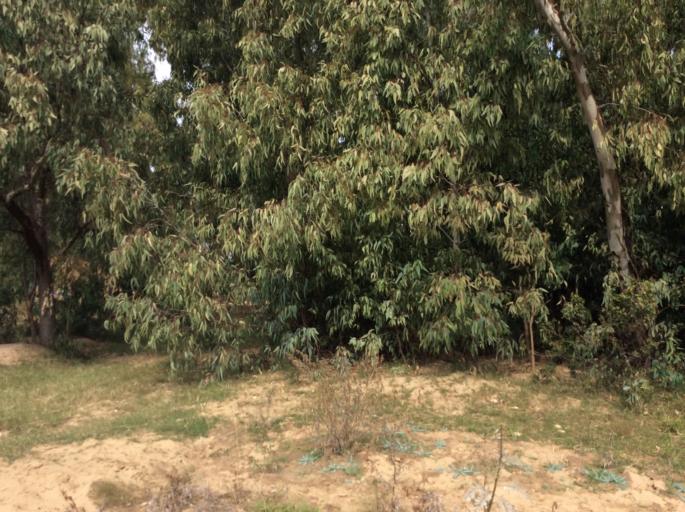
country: LS
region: Mafeteng
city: Mafeteng
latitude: -29.7264
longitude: 27.0313
